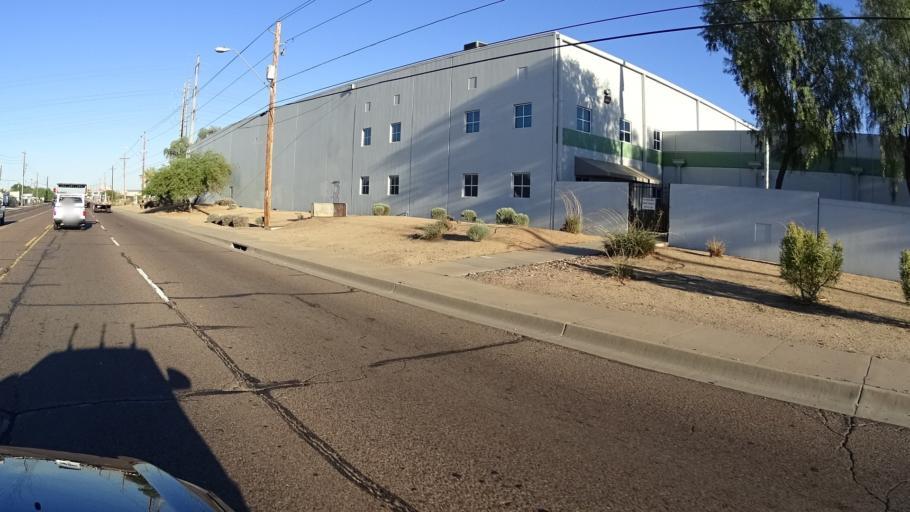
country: US
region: Arizona
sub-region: Maricopa County
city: Laveen
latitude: 33.4369
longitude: -112.1587
